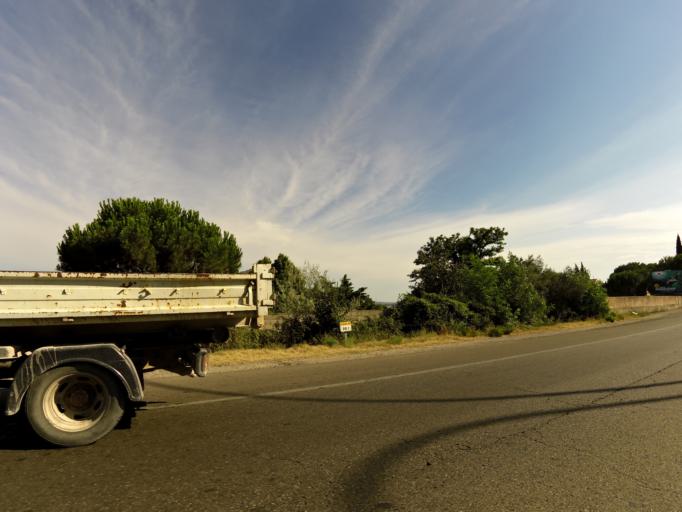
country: FR
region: Languedoc-Roussillon
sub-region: Departement du Gard
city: Nimes
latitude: 43.8211
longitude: 4.3237
